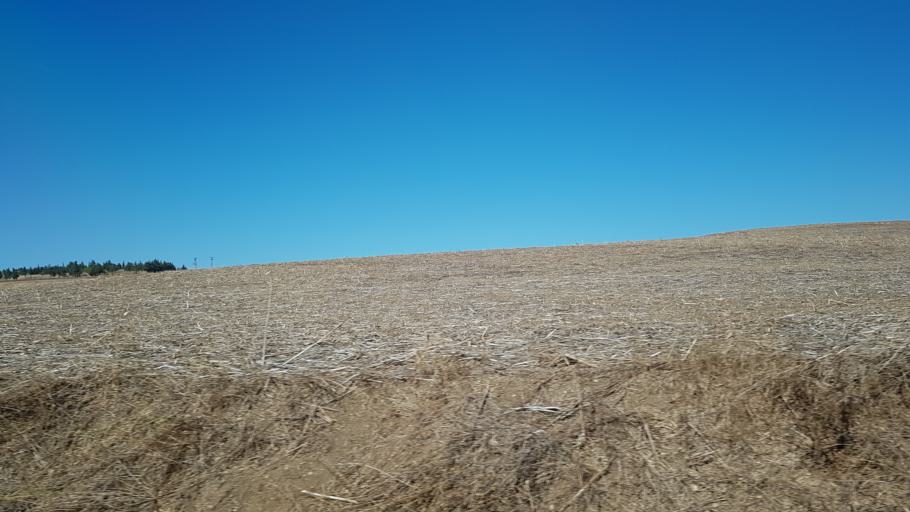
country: TR
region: Tekirdag
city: Corlu
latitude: 41.0325
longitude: 27.8145
